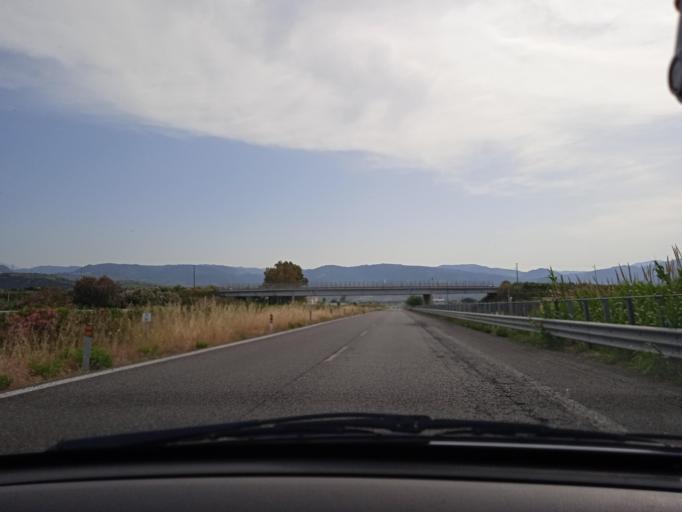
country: IT
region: Sicily
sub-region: Messina
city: Vigliatore 2
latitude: 38.1303
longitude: 15.1319
